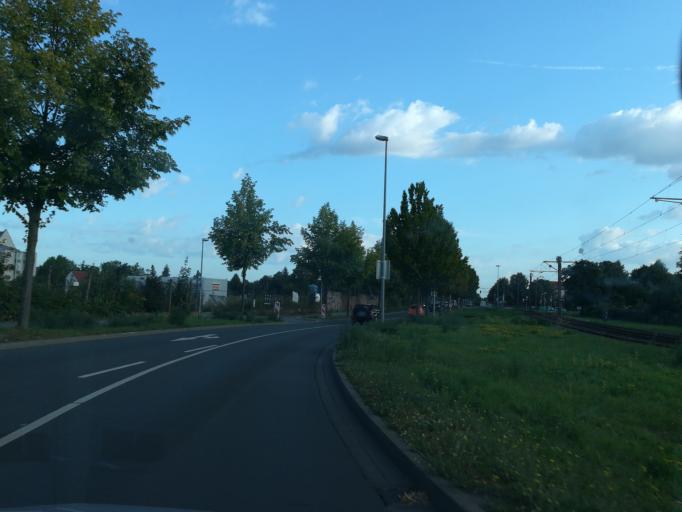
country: DE
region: Saxony-Anhalt
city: Magdeburg
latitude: 52.1363
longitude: 11.6032
